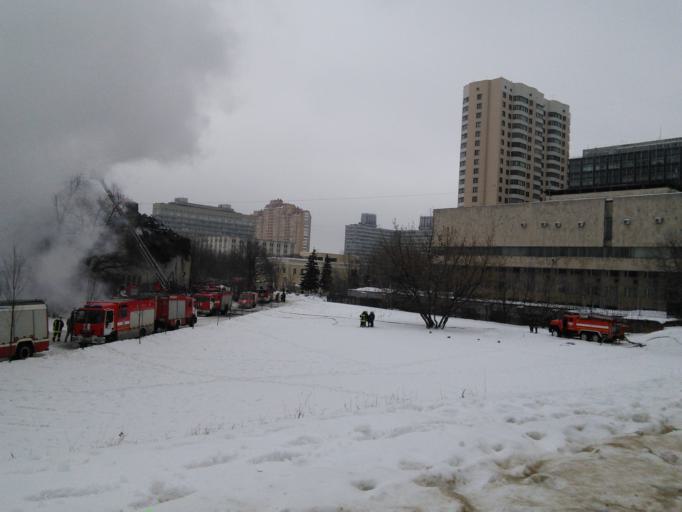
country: RU
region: Moskovskaya
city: Cheremushki
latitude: 55.6753
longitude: 37.5630
